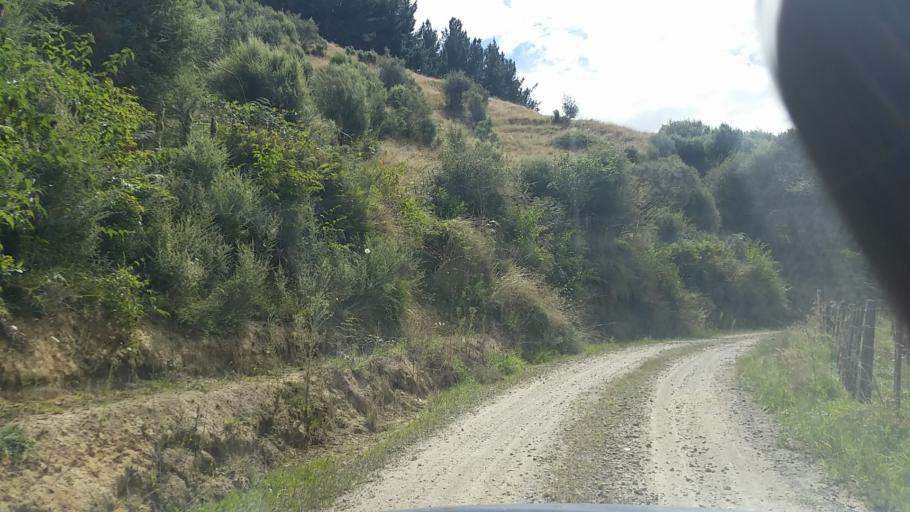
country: NZ
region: Taranaki
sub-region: South Taranaki District
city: Eltham
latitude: -39.2521
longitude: 174.5658
